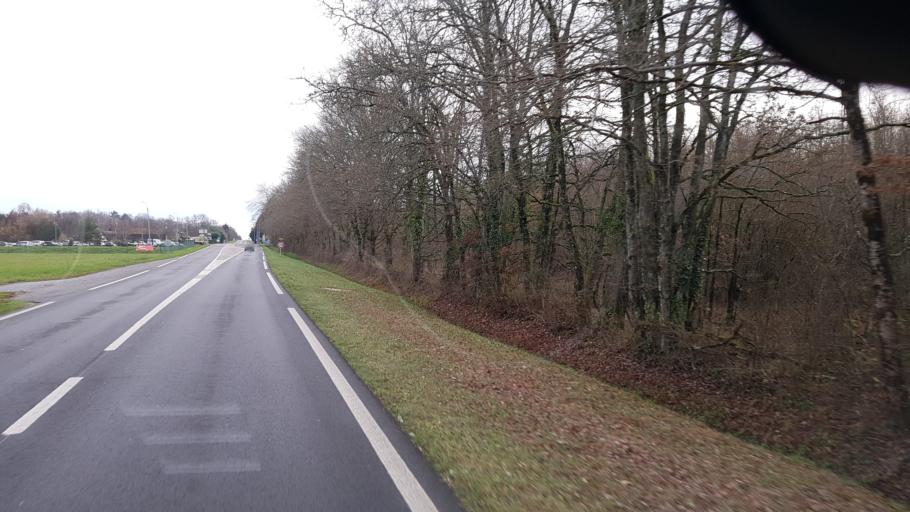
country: FR
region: Centre
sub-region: Departement du Loiret
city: Menestreau-en-Villette
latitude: 47.6546
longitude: 1.9858
